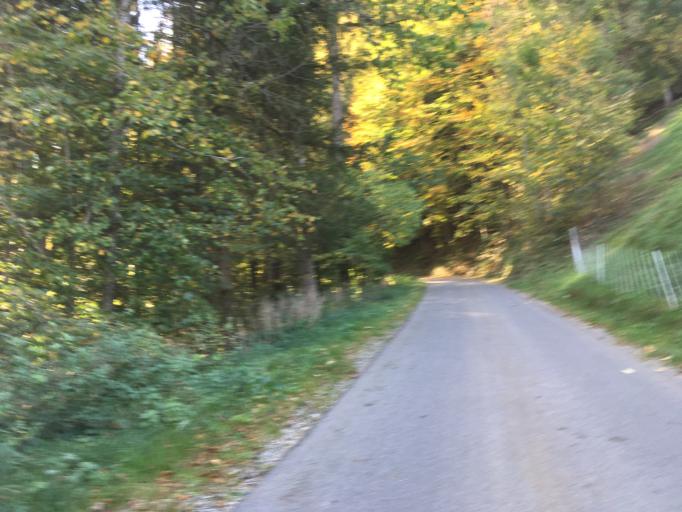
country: CH
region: Saint Gallen
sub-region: Wahlkreis Toggenburg
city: Oberhelfenschwil
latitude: 47.3562
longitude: 9.1194
